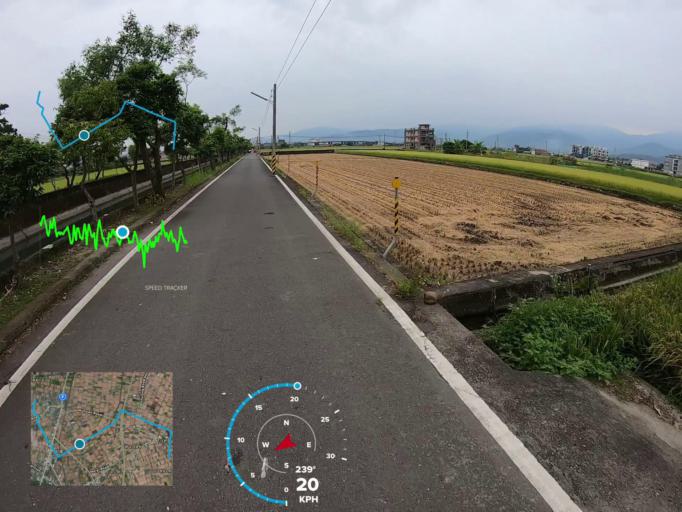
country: TW
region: Taiwan
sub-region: Yilan
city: Yilan
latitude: 24.7786
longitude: 121.7687
